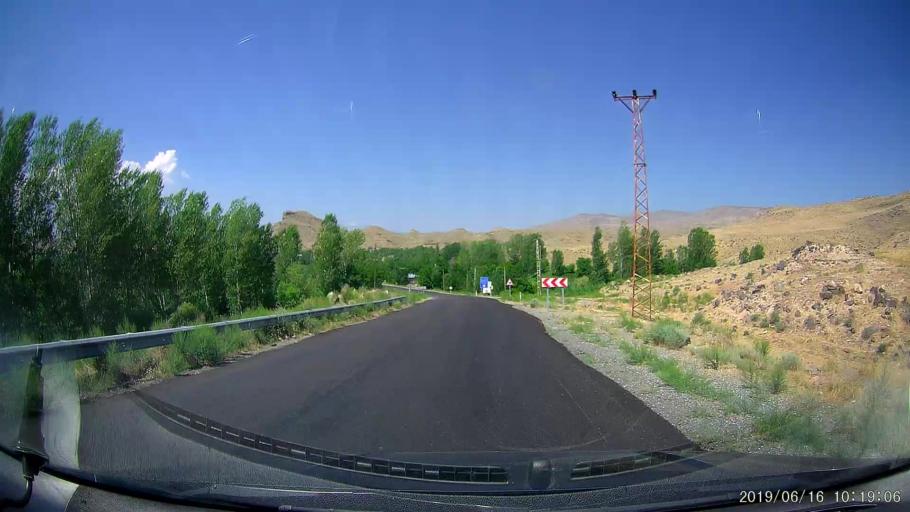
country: TR
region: Igdir
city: Tuzluca
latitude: 40.1562
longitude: 43.6600
